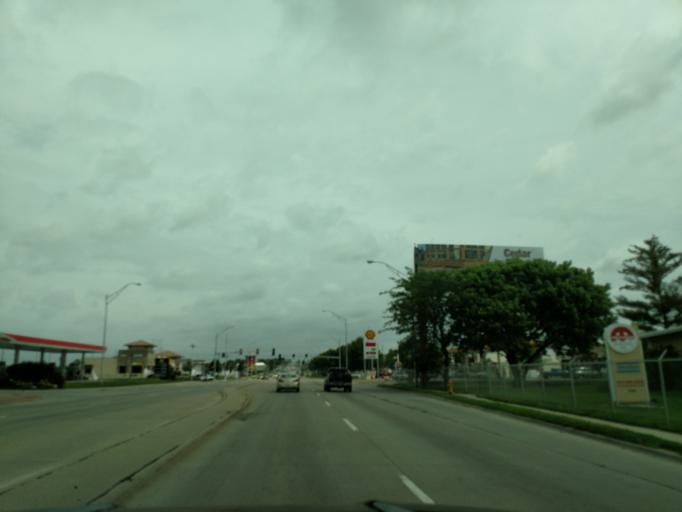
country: US
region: Nebraska
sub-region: Douglas County
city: Ralston
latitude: 41.2040
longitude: -96.0237
